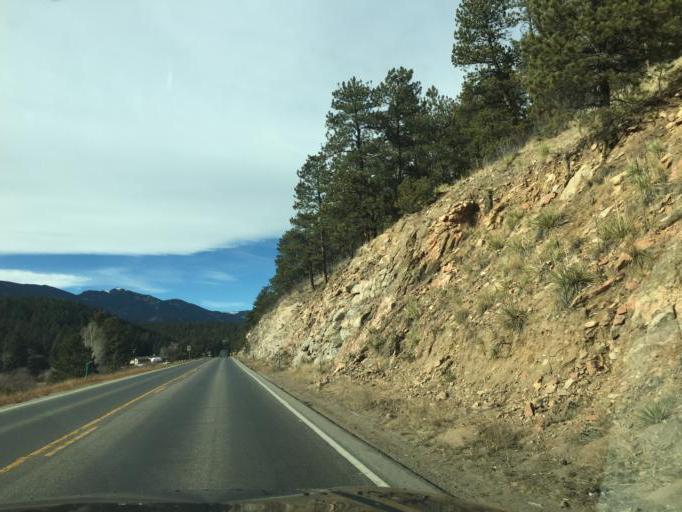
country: US
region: Colorado
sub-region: Jefferson County
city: Evergreen
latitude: 39.4070
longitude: -105.4827
